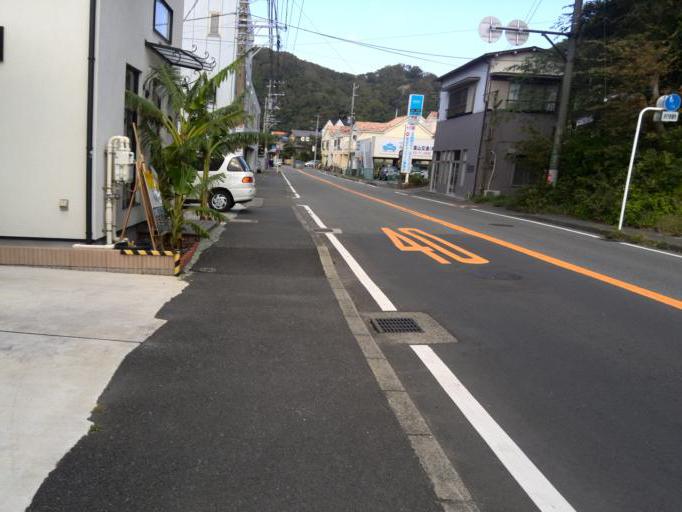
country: JP
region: Kanagawa
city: Hayama
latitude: 35.2787
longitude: 139.5791
